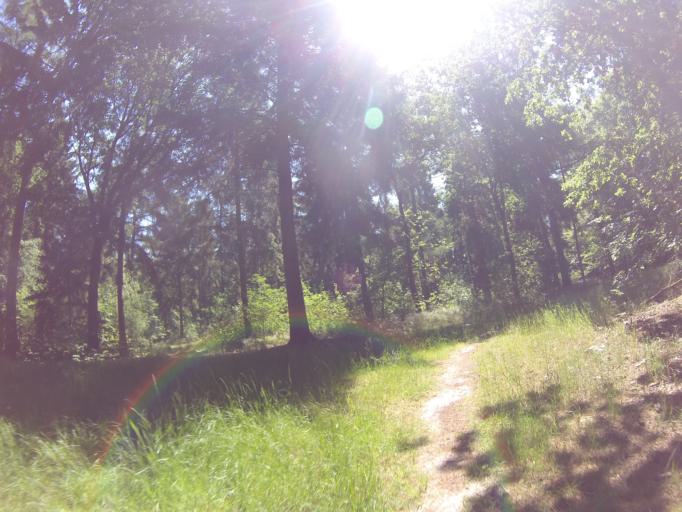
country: NL
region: Drenthe
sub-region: Gemeente Coevorden
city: Sleen
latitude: 52.7626
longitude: 6.8518
